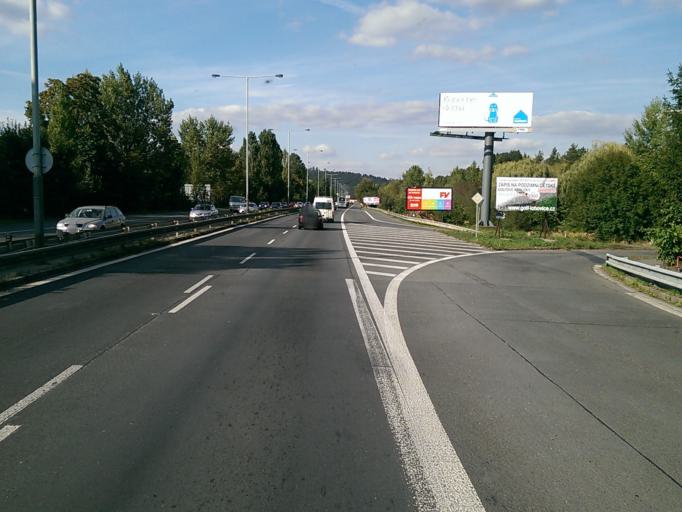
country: CZ
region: Praha
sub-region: Praha 12
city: Modrany
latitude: 50.0031
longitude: 14.3952
